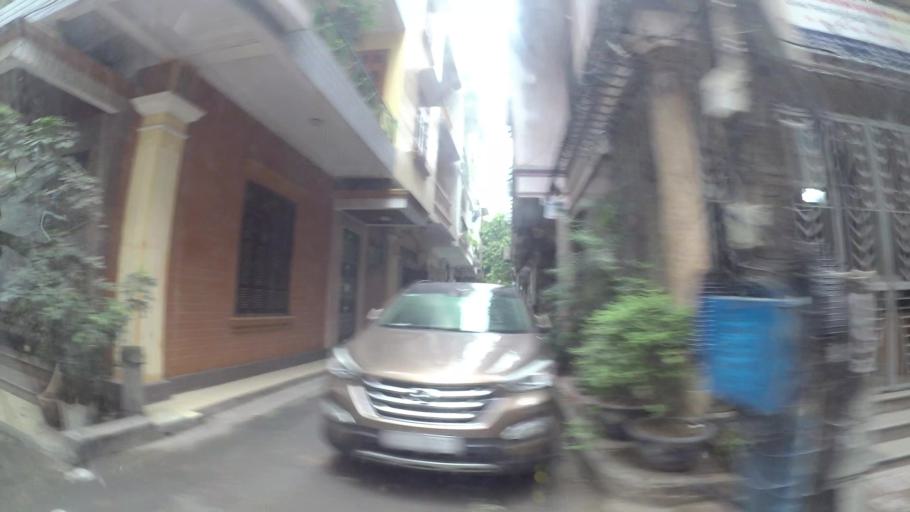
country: VN
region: Ha Noi
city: Dong Da
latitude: 21.0160
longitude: 105.8253
